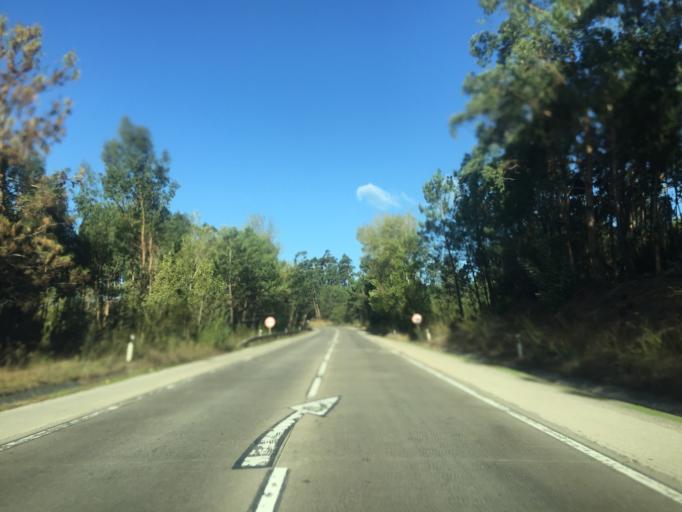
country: PT
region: Santarem
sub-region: Rio Maior
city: Rio Maior
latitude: 39.3208
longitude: -8.9415
